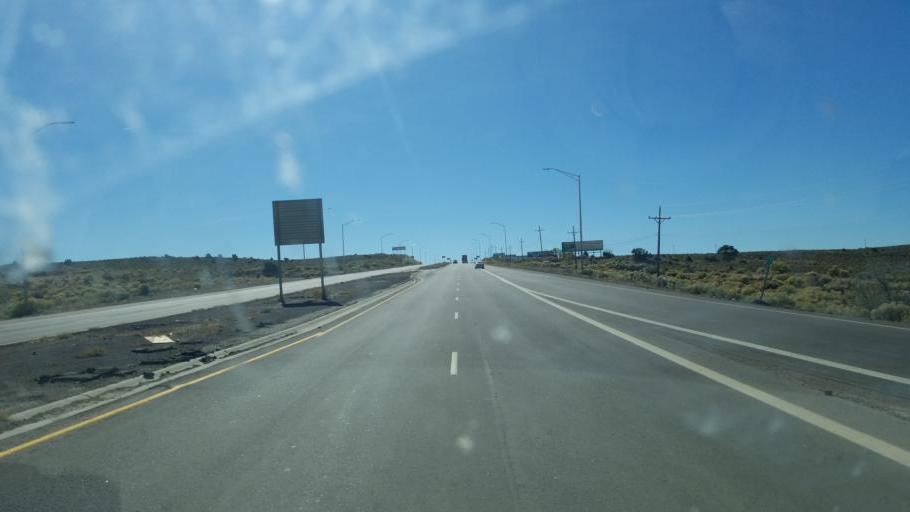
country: US
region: New Mexico
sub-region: McKinley County
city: Twin Lakes
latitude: 35.6230
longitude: -108.7805
